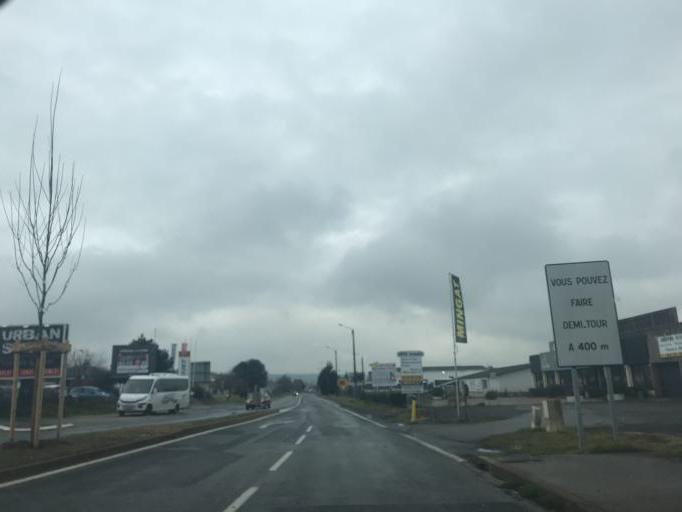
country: FR
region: Rhone-Alpes
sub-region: Departement du Rhone
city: Genay
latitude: 45.8949
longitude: 4.8214
